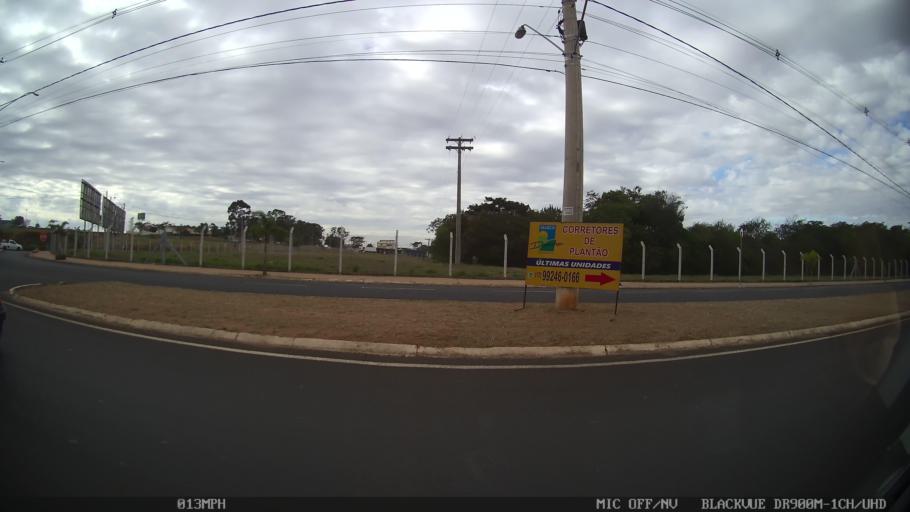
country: BR
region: Sao Paulo
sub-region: Sao Jose Do Rio Preto
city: Sao Jose do Rio Preto
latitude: -20.8143
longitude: -49.4816
